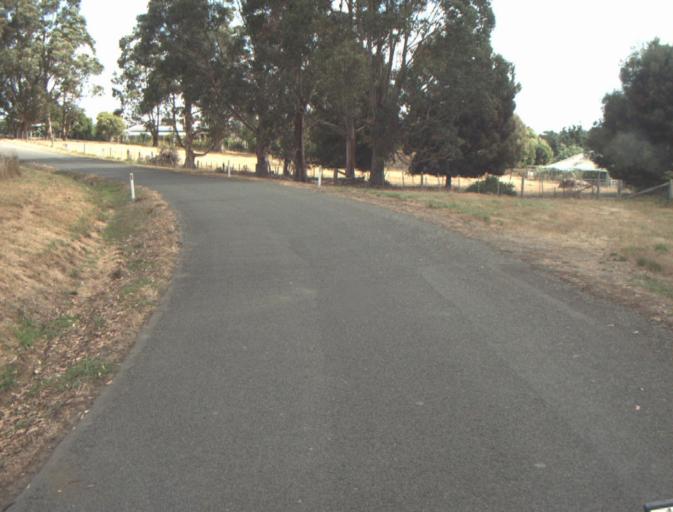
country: AU
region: Tasmania
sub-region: Launceston
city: Mayfield
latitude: -41.2961
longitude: 146.9878
